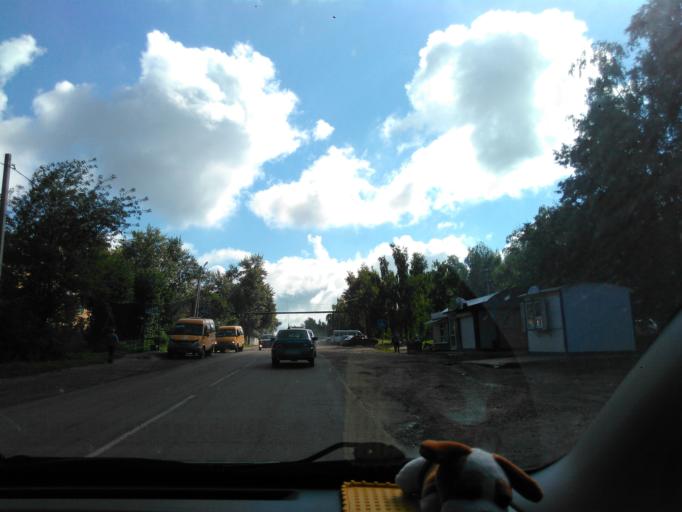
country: RU
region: Penza
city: Lermontovo
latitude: 53.1882
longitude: 44.0670
